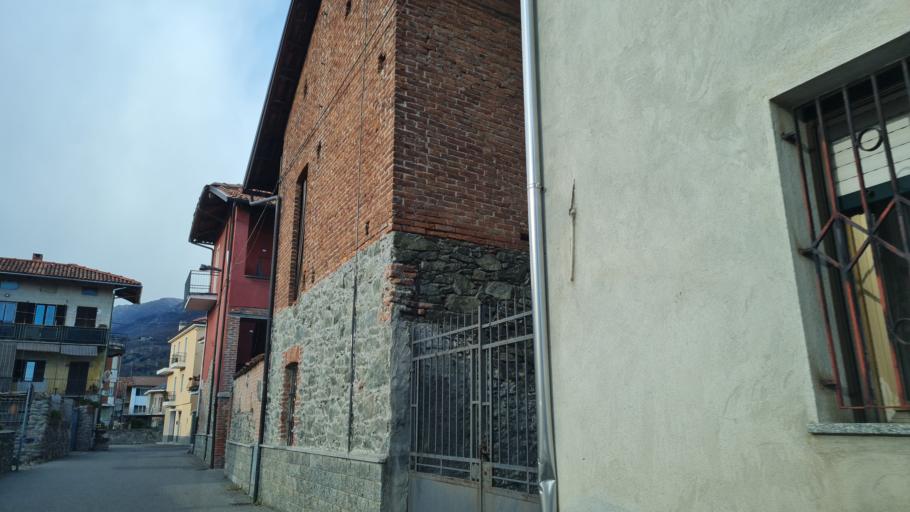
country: IT
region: Piedmont
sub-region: Provincia di Torino
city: Borgofranco d'Ivrea
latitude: 45.5123
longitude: 7.8604
